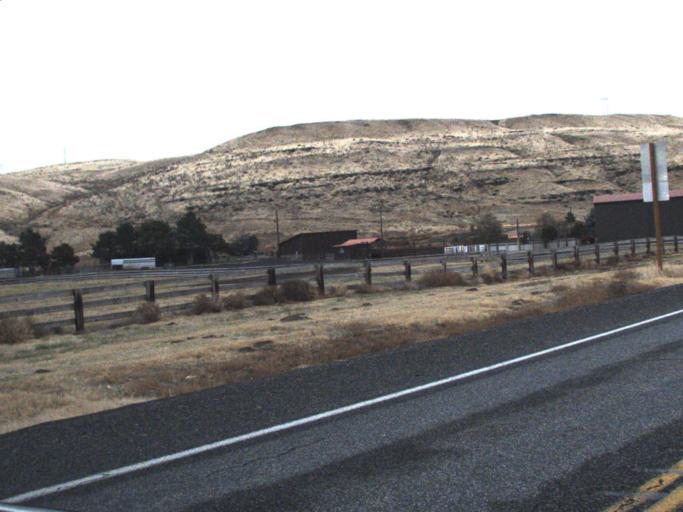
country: US
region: Washington
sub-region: Walla Walla County
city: Burbank
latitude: 46.0725
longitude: -118.7884
